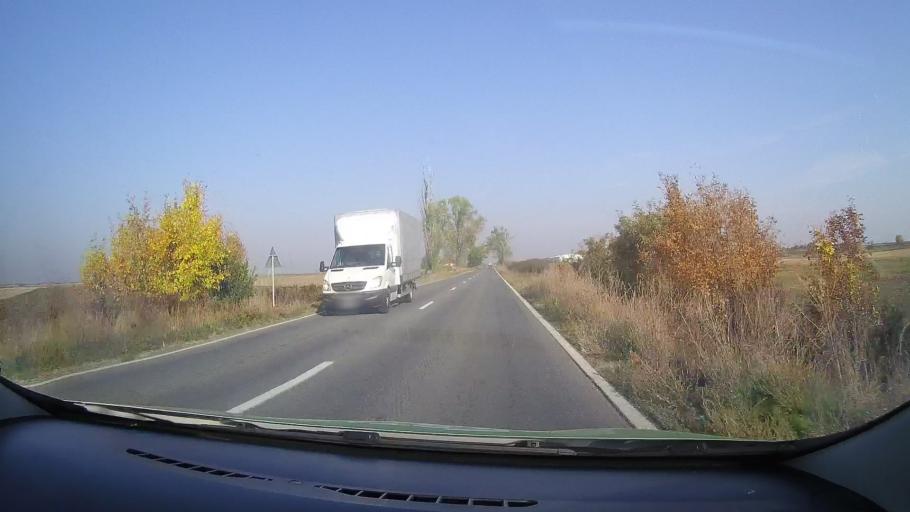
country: RO
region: Arad
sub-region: Comuna Pilu
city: Pilu
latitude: 46.5644
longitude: 21.3458
